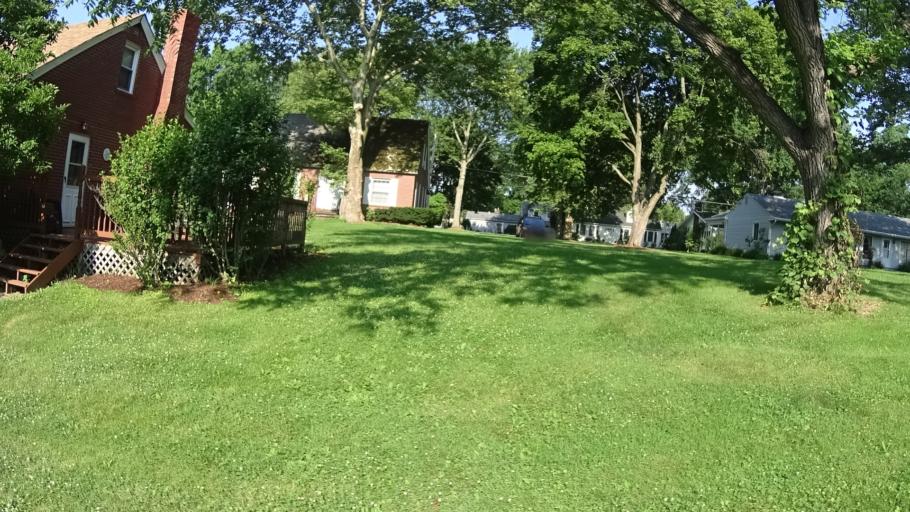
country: US
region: Ohio
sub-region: Lorain County
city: Vermilion
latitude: 41.3870
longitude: -82.4542
